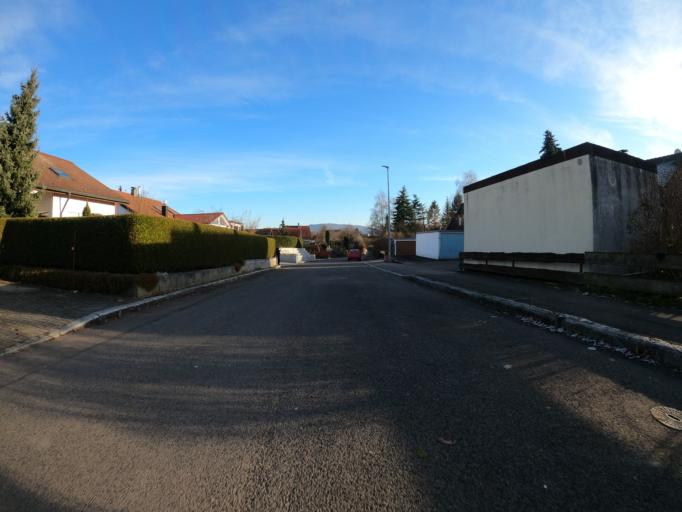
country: DE
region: Baden-Wuerttemberg
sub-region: Regierungsbezirk Stuttgart
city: Boll
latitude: 48.6725
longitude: 9.6083
